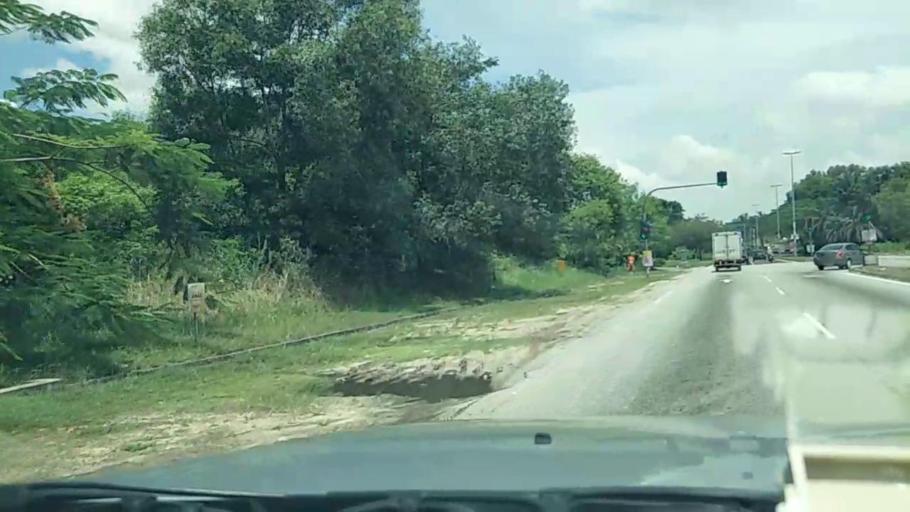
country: MY
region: Selangor
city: Subang Jaya
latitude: 2.9693
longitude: 101.6136
